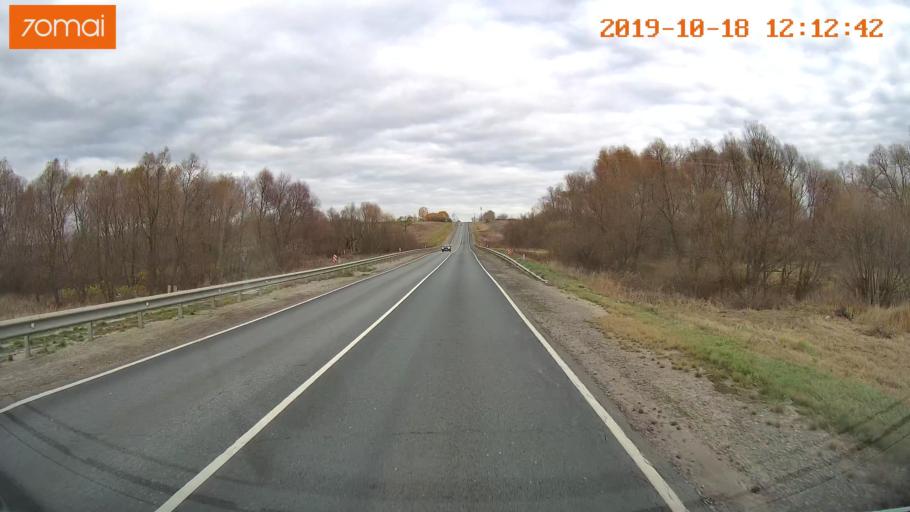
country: RU
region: Rjazan
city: Zakharovo
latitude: 54.4143
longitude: 39.3612
